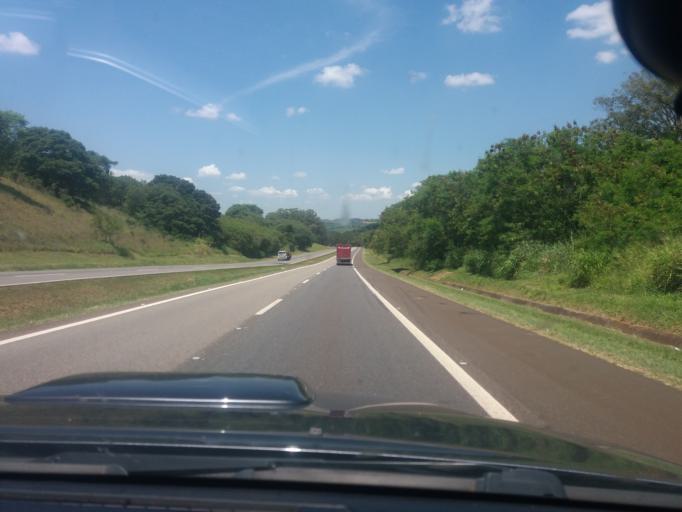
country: BR
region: Sao Paulo
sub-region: Tatui
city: Tatui
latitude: -23.3676
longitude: -47.9077
